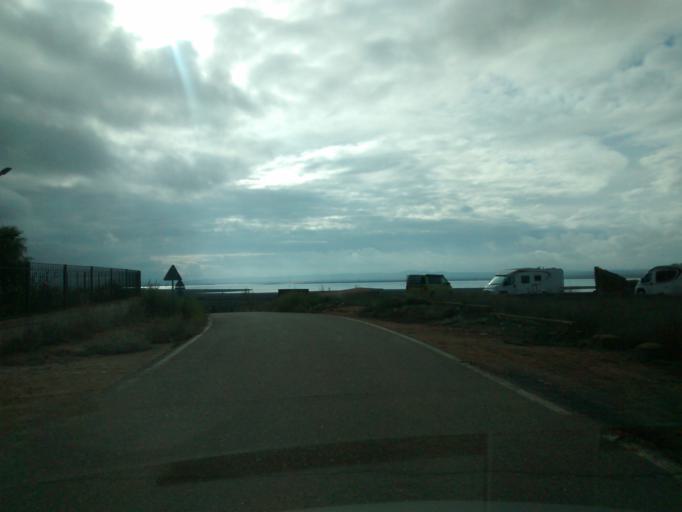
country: ES
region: Aragon
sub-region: Provincia de Zaragoza
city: Gallocanta
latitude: 40.9951
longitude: -1.5067
